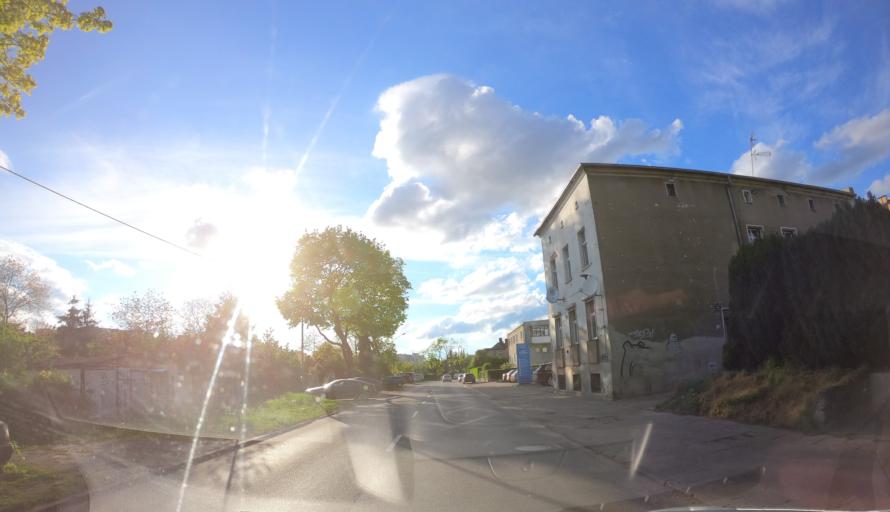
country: PL
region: West Pomeranian Voivodeship
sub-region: Szczecin
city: Szczecin
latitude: 53.4137
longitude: 14.5390
